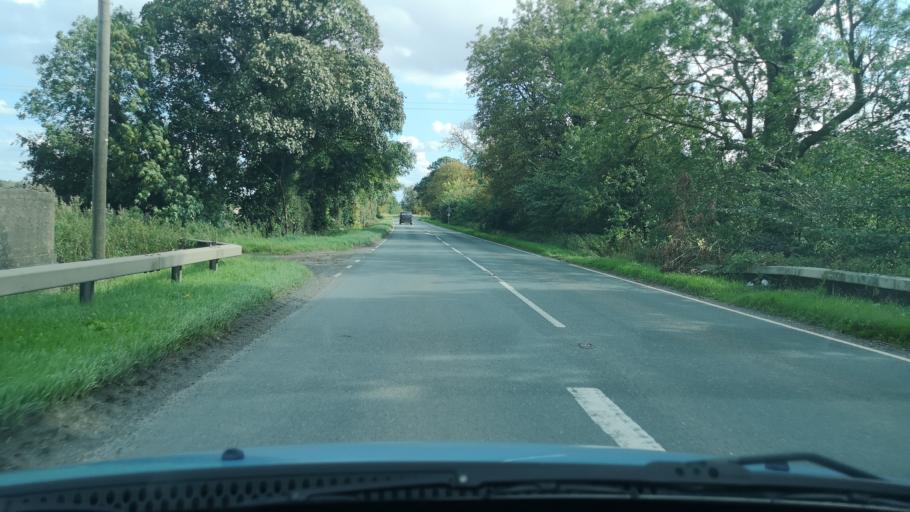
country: GB
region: England
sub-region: North Lincolnshire
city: Belton
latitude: 53.5785
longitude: -0.8204
